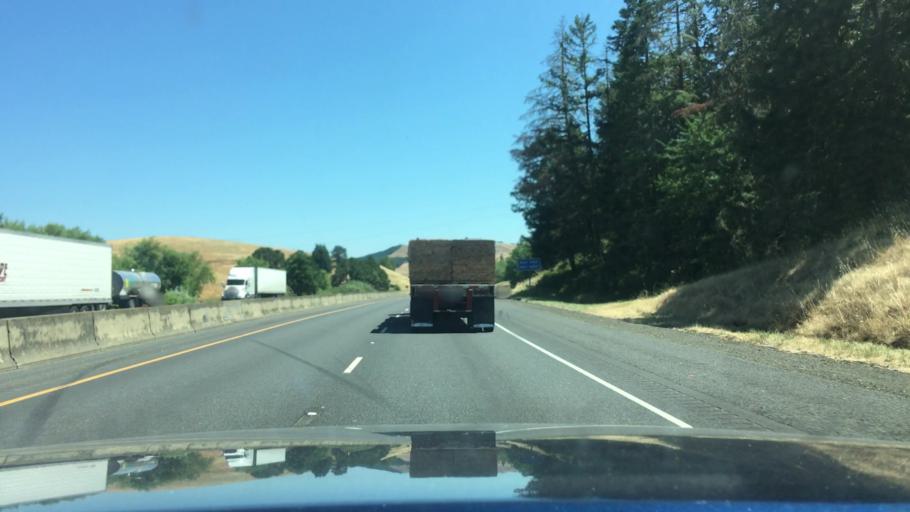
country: US
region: Oregon
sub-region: Douglas County
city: Sutherlin
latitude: 43.4844
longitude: -123.3256
